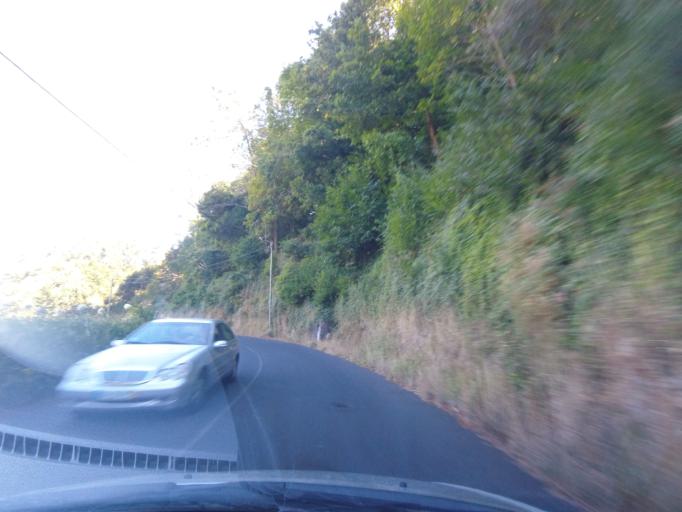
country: PT
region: Madeira
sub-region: Santa Cruz
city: Camacha
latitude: 32.6860
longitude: -16.8525
